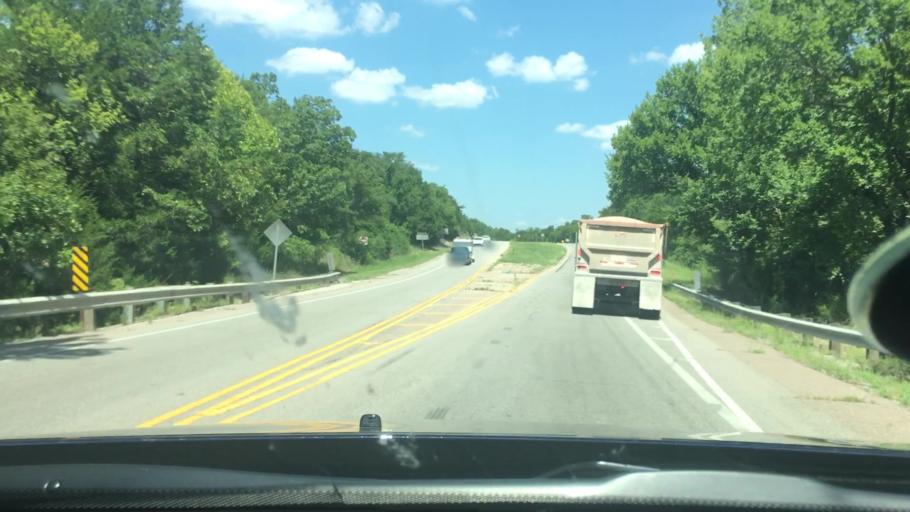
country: US
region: Oklahoma
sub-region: Marshall County
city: Oakland
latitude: 34.1677
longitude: -96.8317
